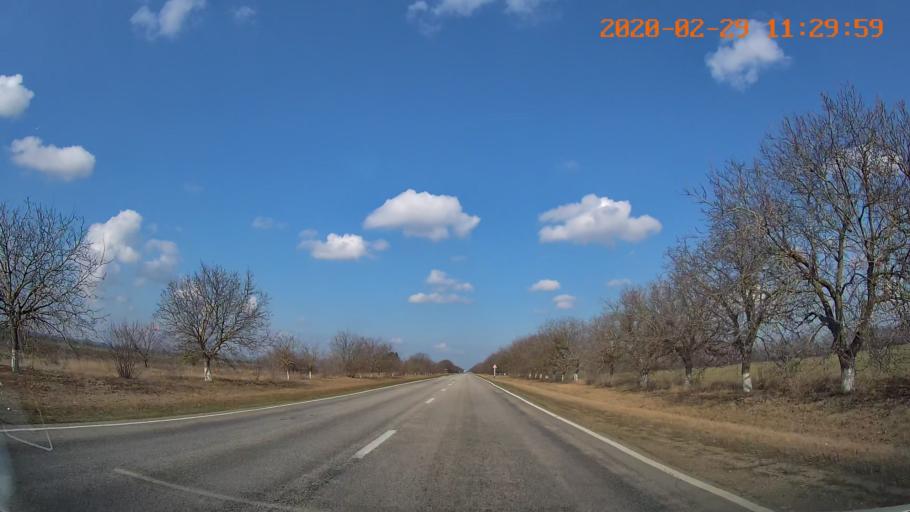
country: MD
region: Telenesti
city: Cocieri
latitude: 47.5030
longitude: 29.1199
